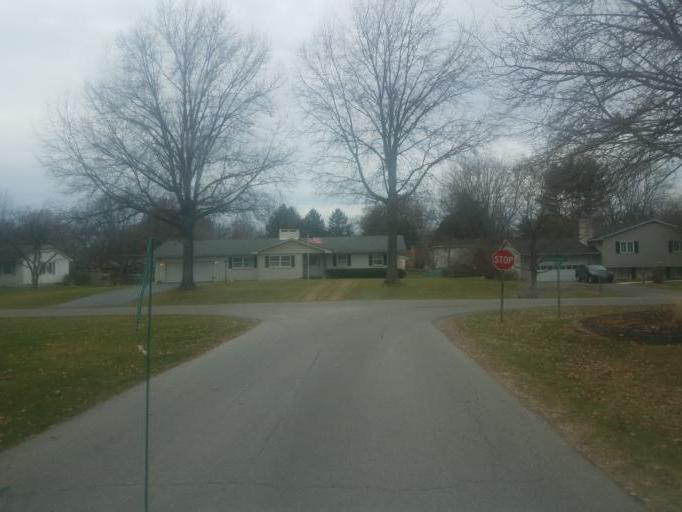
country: US
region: Ohio
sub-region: Marion County
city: Marion
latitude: 40.5671
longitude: -83.0796
